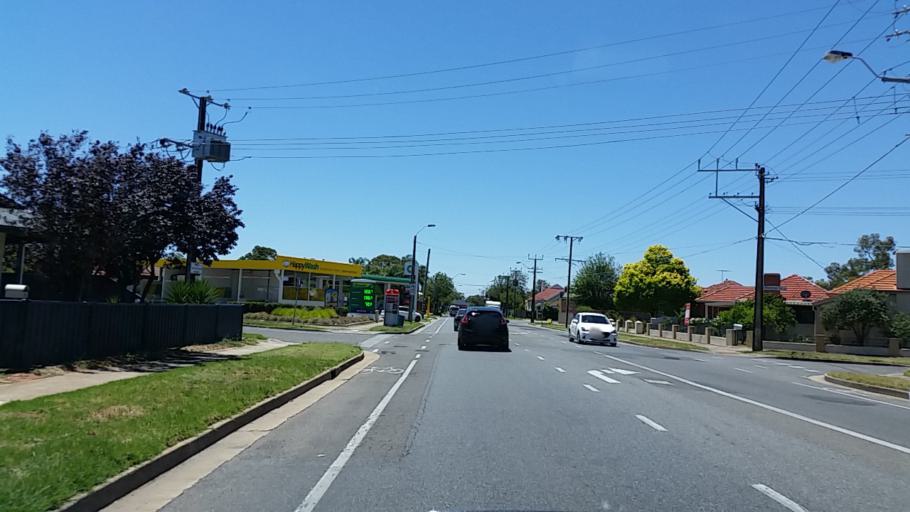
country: AU
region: South Australia
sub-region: Charles Sturt
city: Woodville
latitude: -34.8819
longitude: 138.5497
